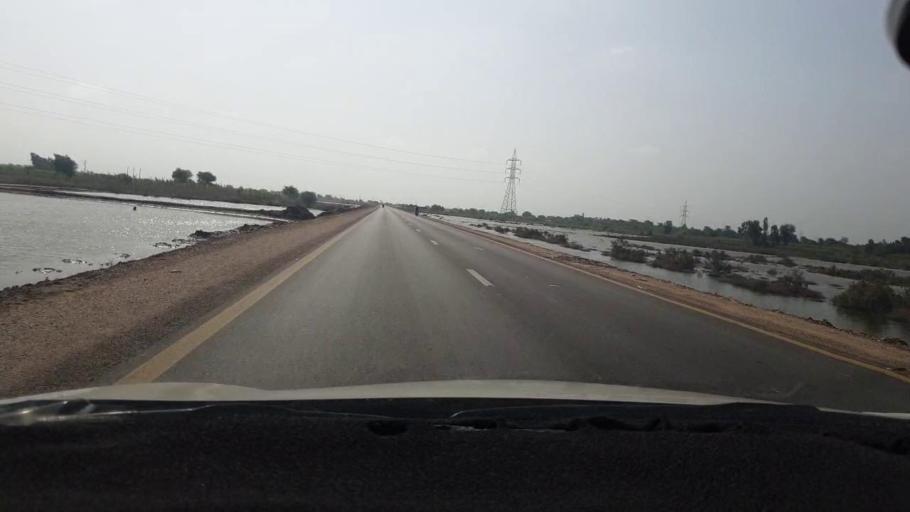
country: PK
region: Sindh
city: Jhol
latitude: 25.8644
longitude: 69.0536
